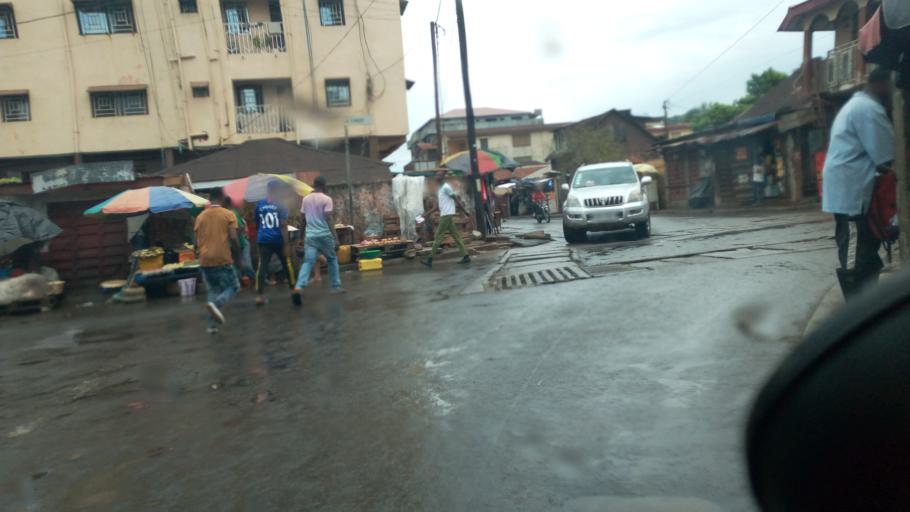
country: SL
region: Western Area
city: Freetown
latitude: 8.4758
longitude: -13.2393
